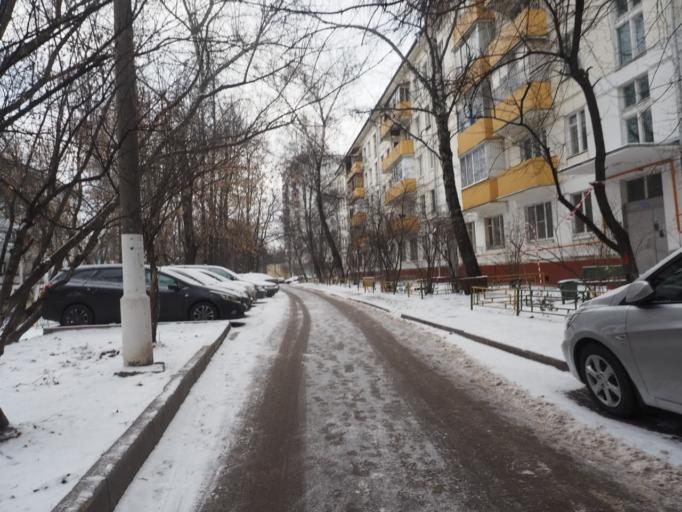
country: RU
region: Moscow
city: Orekhovo-Borisovo Severnoye
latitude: 55.6270
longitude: 37.6767
